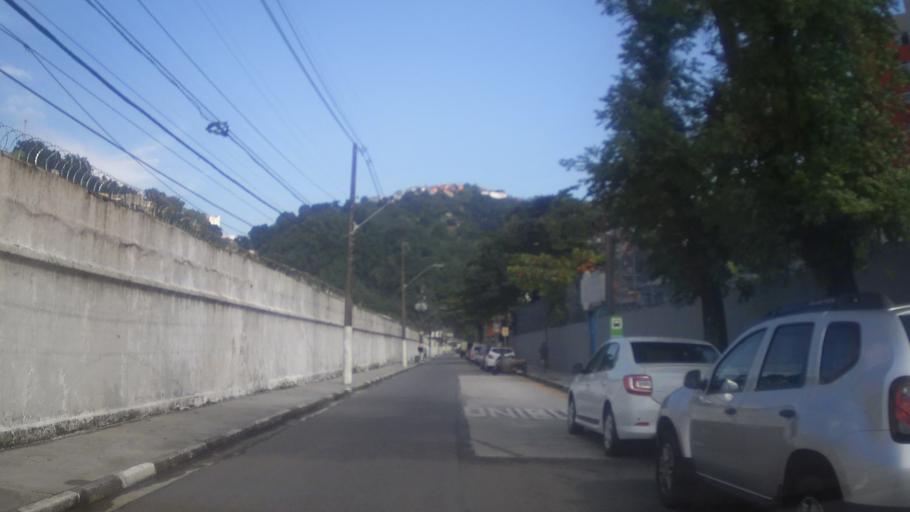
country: BR
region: Sao Paulo
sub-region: Santos
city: Santos
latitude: -23.9314
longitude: -46.3475
